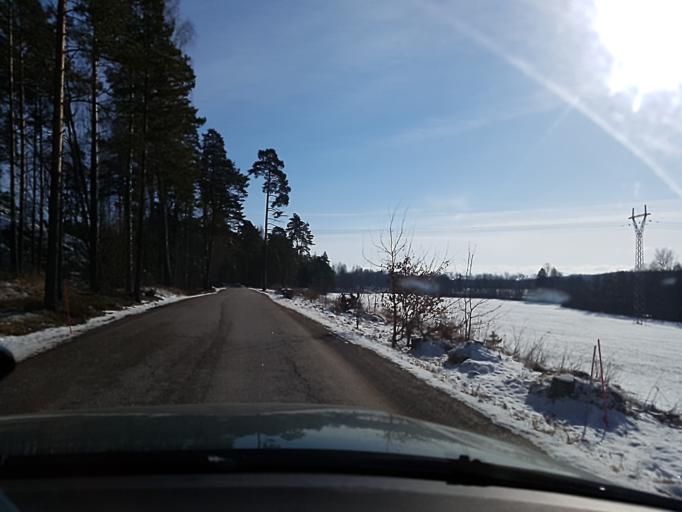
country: FI
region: Uusimaa
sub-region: Helsinki
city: Siuntio
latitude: 60.1042
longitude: 24.2927
